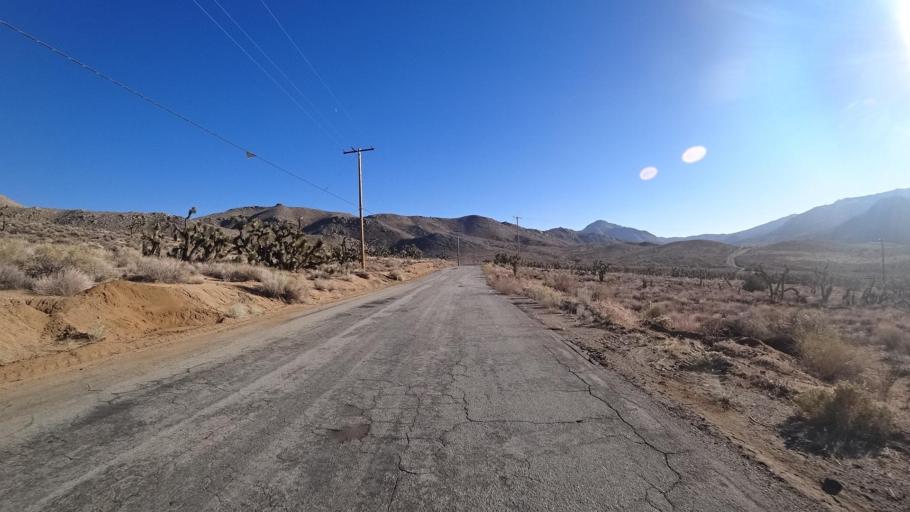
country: US
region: California
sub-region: Kern County
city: Weldon
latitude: 35.5290
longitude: -118.2011
